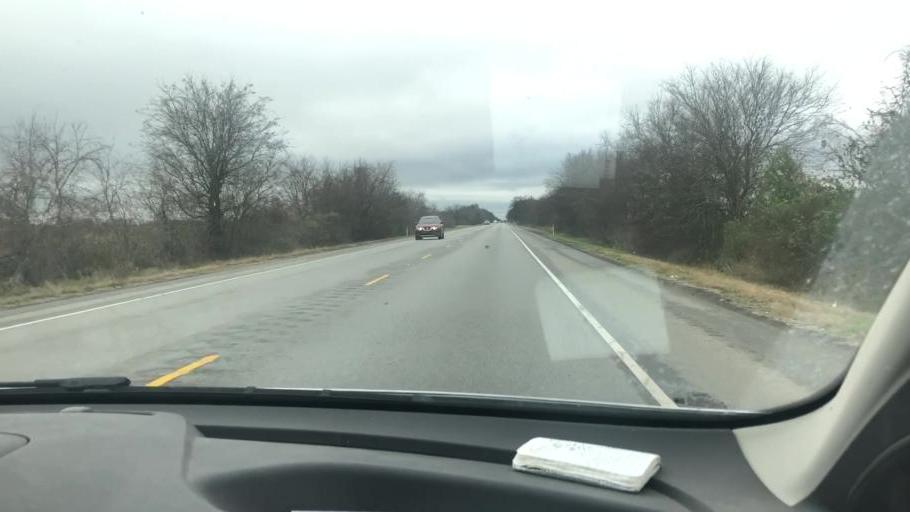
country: US
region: Texas
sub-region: Matagorda County
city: Bay City
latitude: 29.1144
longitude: -95.9797
